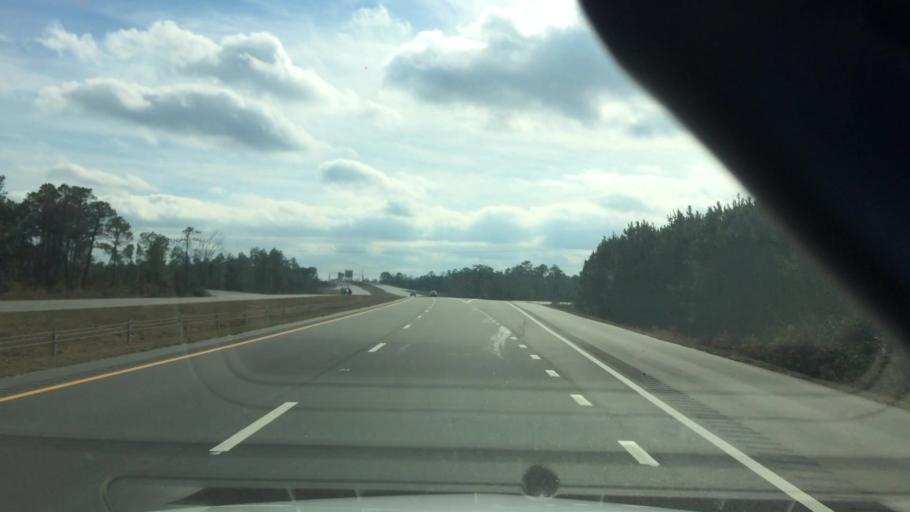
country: US
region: North Carolina
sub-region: Brunswick County
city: Leland
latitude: 34.2646
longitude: -78.0796
